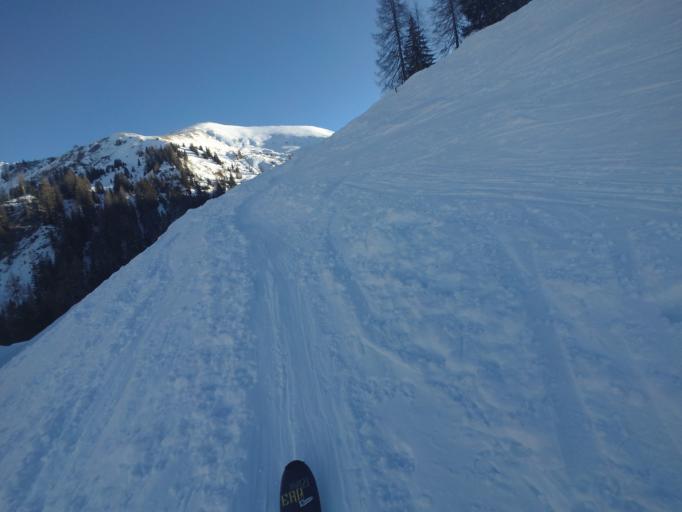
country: AT
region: Salzburg
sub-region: Politischer Bezirk Sankt Johann im Pongau
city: Huttschlag
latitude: 47.1825
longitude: 13.2869
